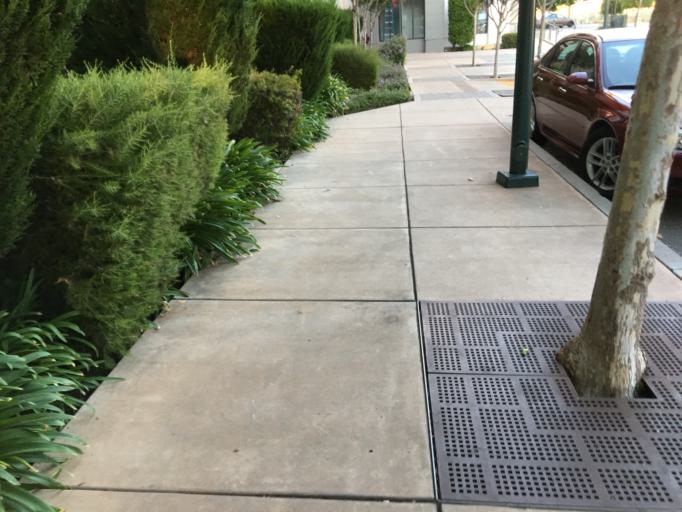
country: US
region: California
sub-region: Alameda County
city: Dublin
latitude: 37.7043
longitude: -121.8981
